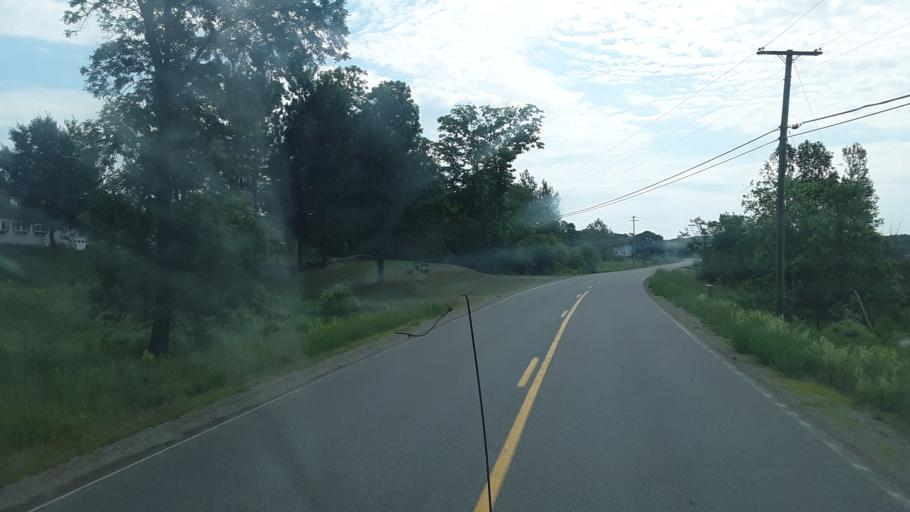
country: US
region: Maine
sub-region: Waldo County
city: Frankfort
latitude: 44.6145
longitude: -68.9306
